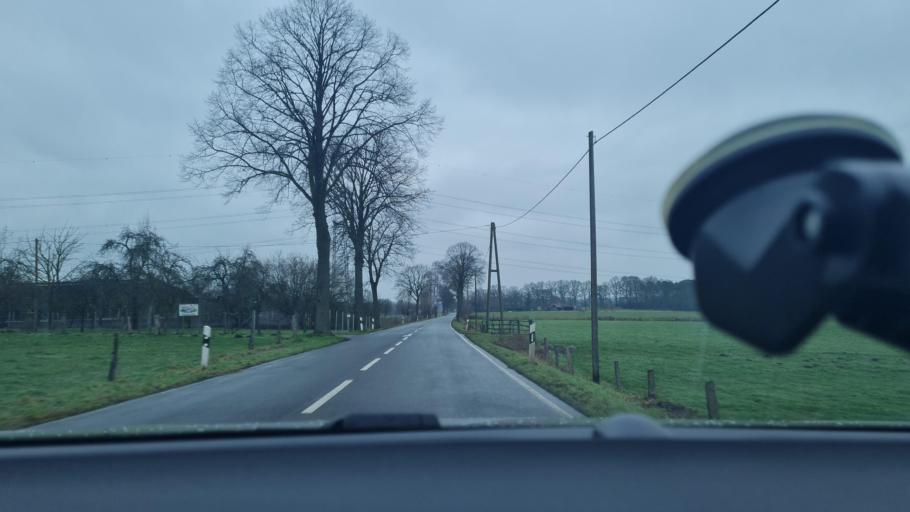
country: DE
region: North Rhine-Westphalia
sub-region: Regierungsbezirk Dusseldorf
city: Hunxe
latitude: 51.7203
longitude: 6.7480
